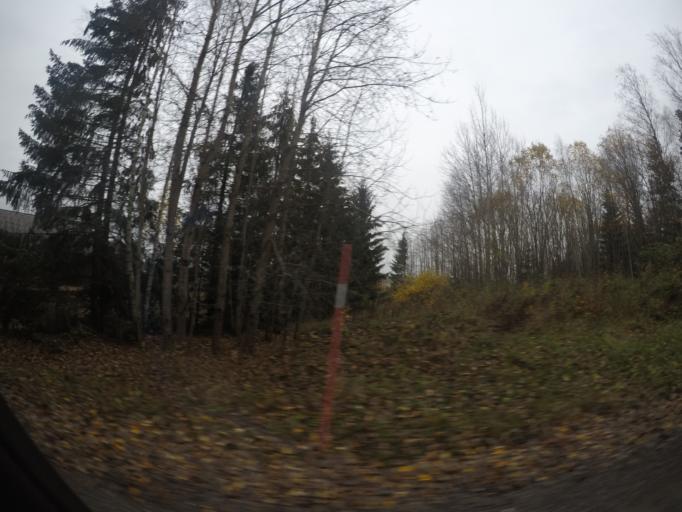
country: SE
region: Vaestmanland
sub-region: Kopings Kommun
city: Koping
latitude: 59.5971
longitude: 16.0791
